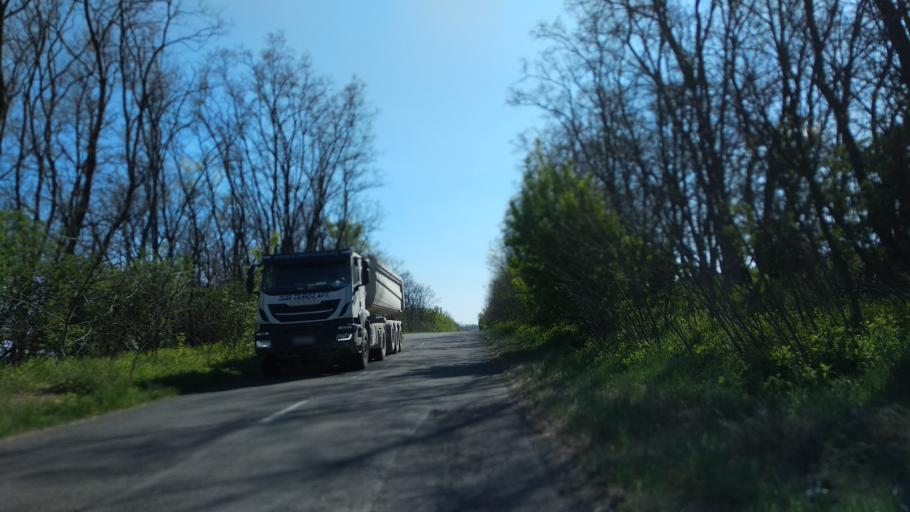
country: HU
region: Pest
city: Godollo
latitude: 47.5849
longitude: 19.3424
